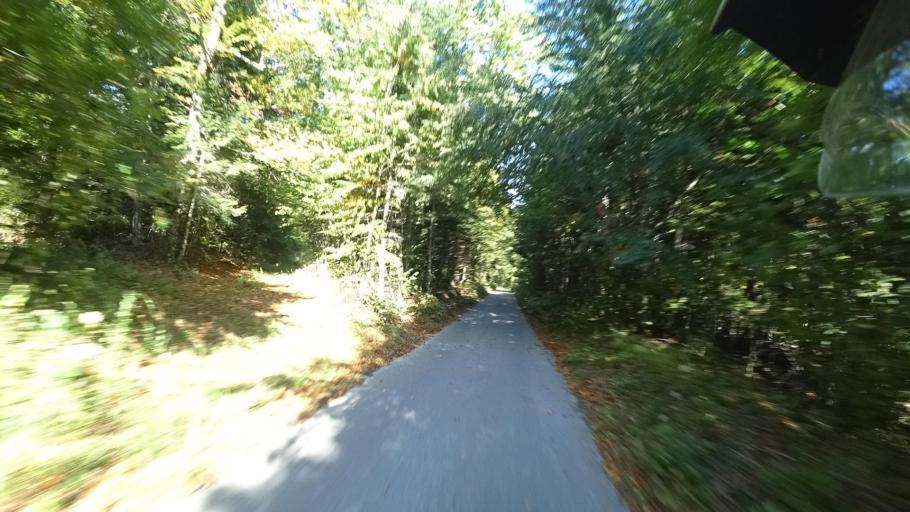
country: HR
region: Karlovacka
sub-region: Grad Ogulin
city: Ogulin
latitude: 45.2392
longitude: 15.1450
